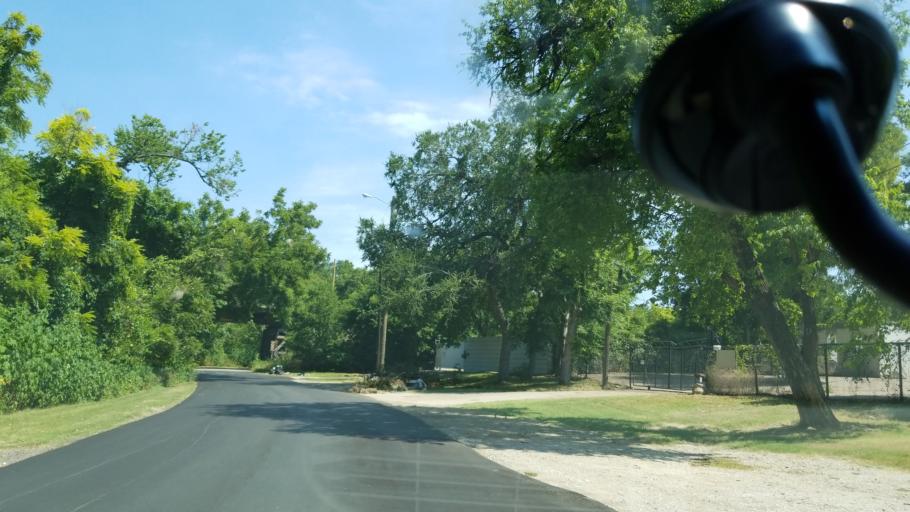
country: US
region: Texas
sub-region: Dallas County
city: Cockrell Hill
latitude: 32.7152
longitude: -96.8812
